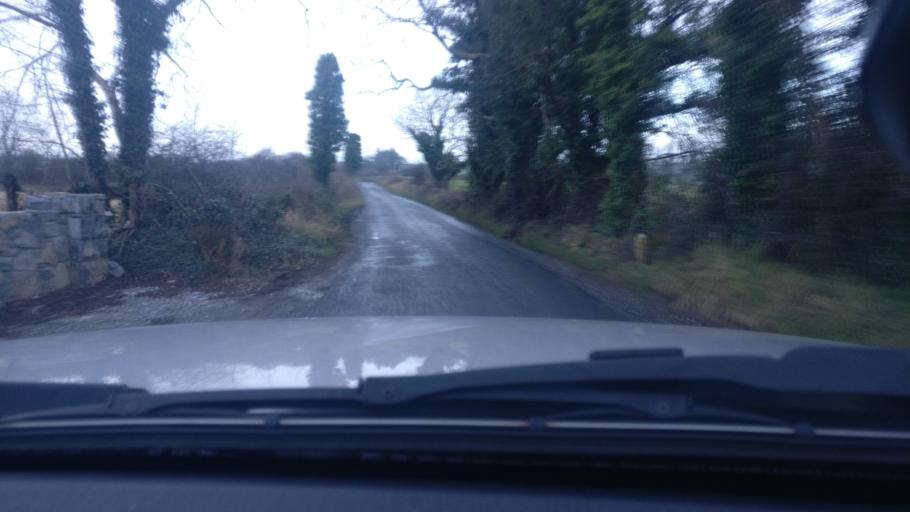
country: IE
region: Connaught
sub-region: County Galway
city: Loughrea
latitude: 53.1637
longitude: -8.5061
